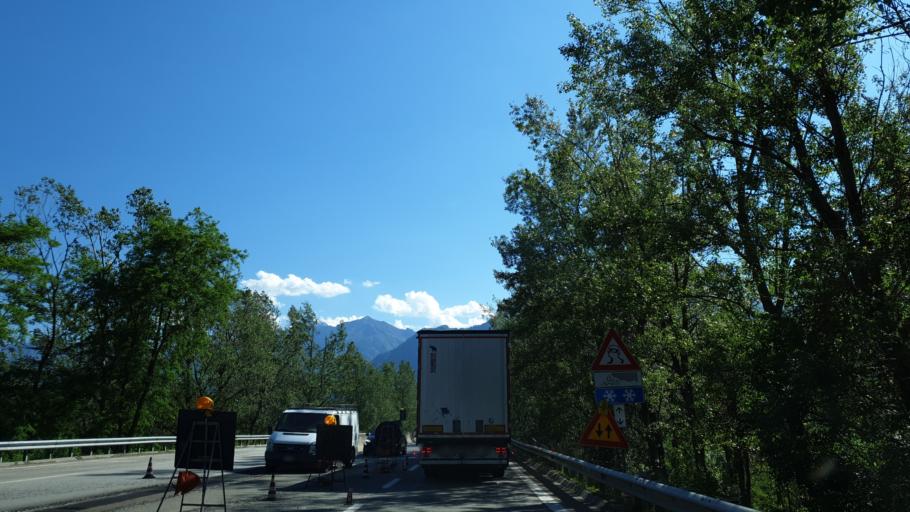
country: IT
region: Piedmont
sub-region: Provincia Verbano-Cusio-Ossola
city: Beura
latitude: 46.0843
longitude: 8.2837
